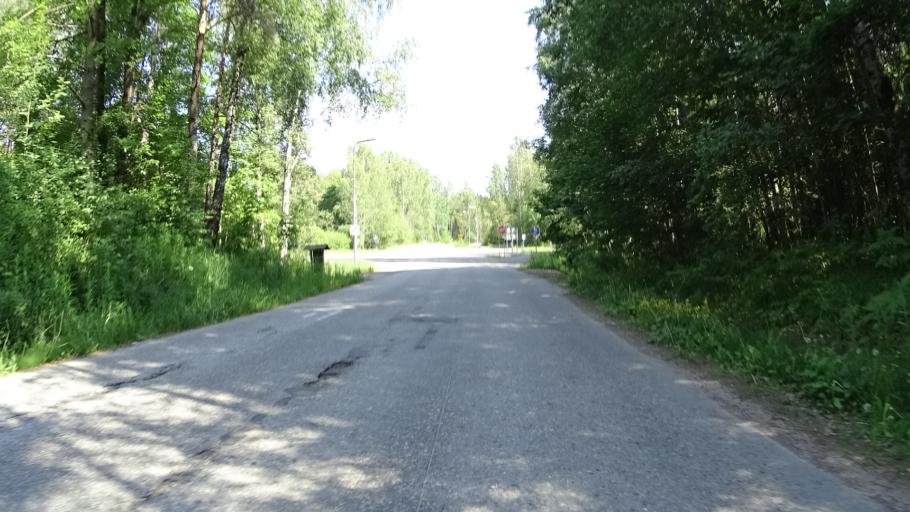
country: FI
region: Uusimaa
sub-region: Raaseporin
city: Karis
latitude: 60.0822
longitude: 23.6604
